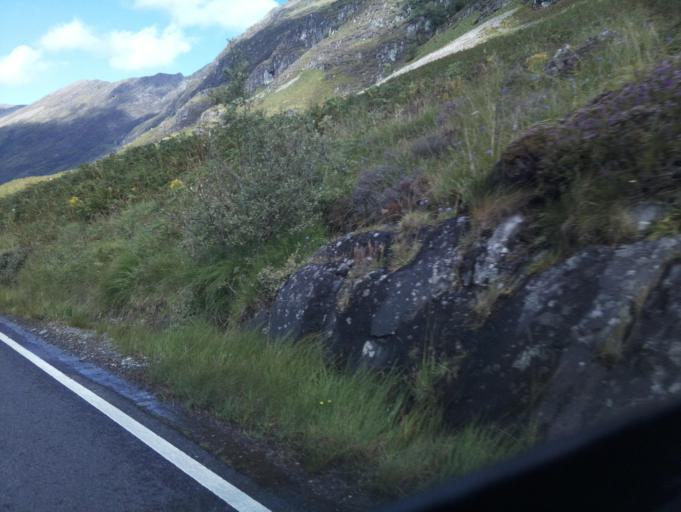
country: GB
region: Scotland
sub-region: Highland
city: Fort William
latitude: 56.6686
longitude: -4.9865
